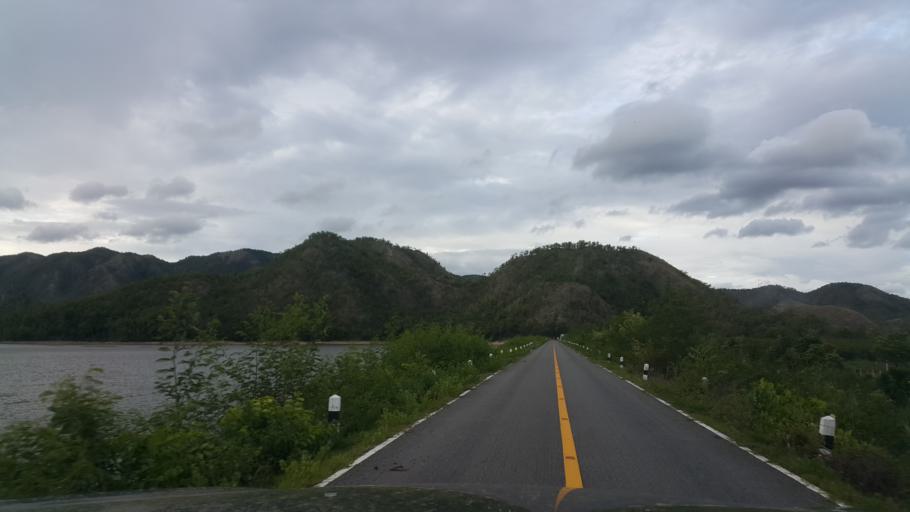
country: TH
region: Sukhothai
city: Thung Saliam
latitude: 17.1758
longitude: 99.4808
